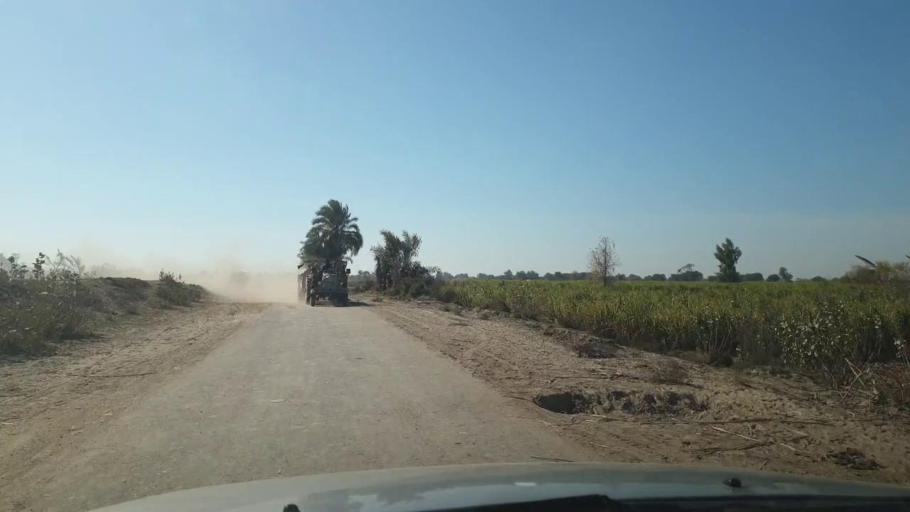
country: PK
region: Sindh
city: Ghotki
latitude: 28.0222
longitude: 69.2684
